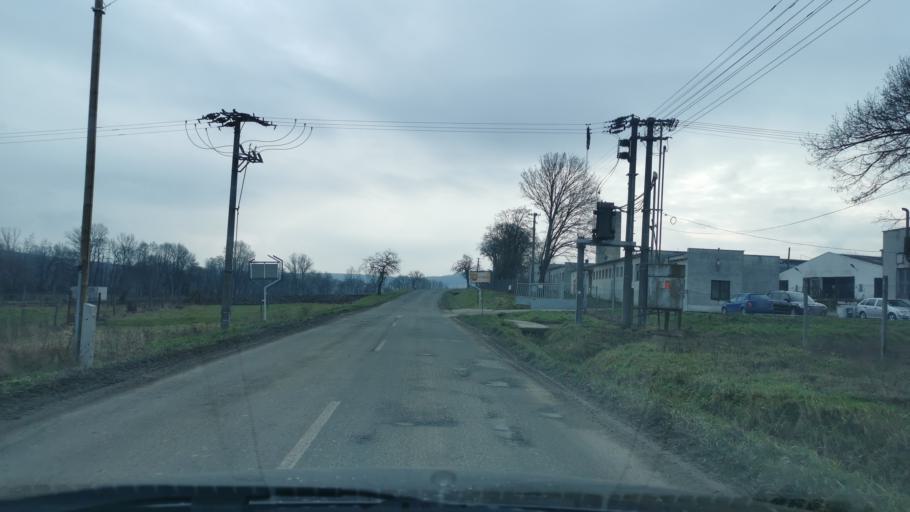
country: SK
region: Trnavsky
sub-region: Okres Skalica
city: Skalica
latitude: 48.7602
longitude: 17.2840
